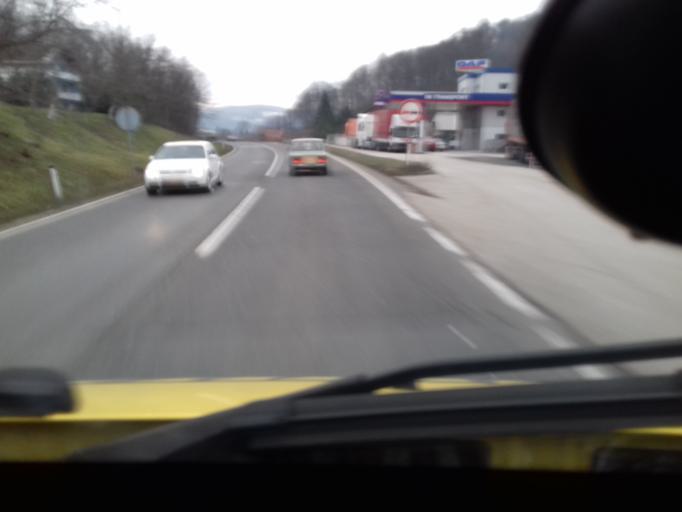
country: BA
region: Federation of Bosnia and Herzegovina
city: Lijesnica
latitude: 44.5021
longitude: 18.0794
